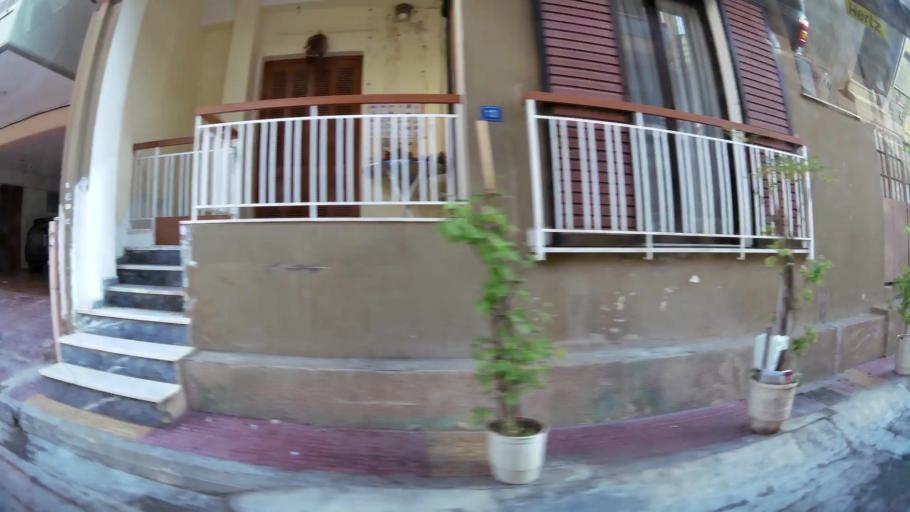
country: GR
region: Attica
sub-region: Nomarchia Athinas
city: Nea Filadelfeia
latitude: 38.0475
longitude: 23.7321
